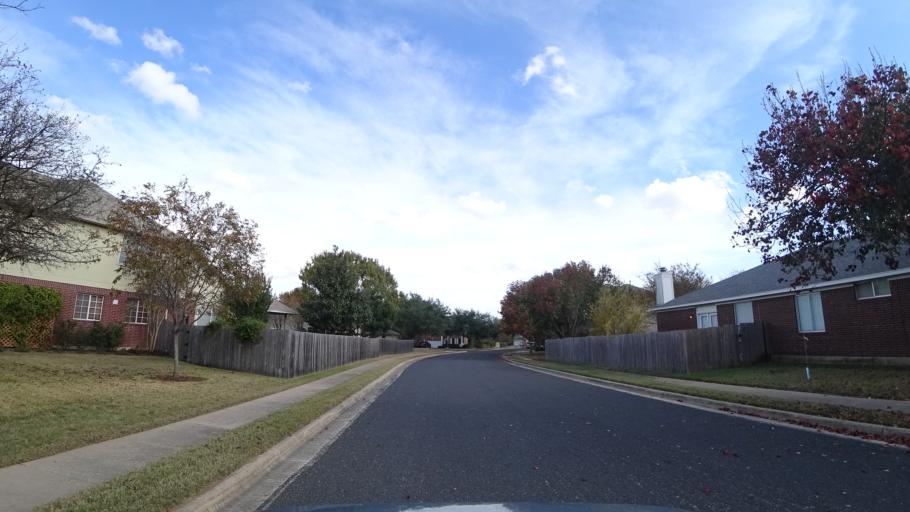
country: US
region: Texas
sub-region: Williamson County
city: Brushy Creek
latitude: 30.5065
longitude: -97.7350
